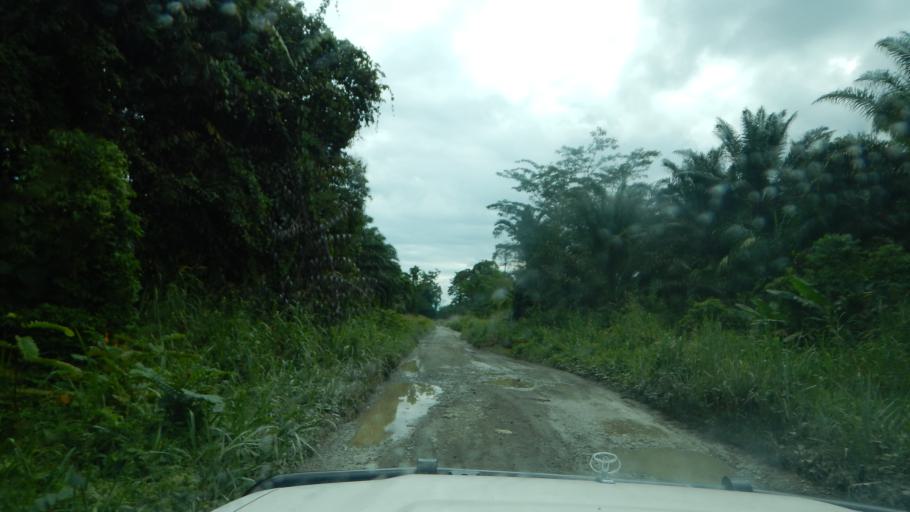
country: PG
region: Northern Province
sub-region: Sohe
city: Kokoda
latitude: -8.9179
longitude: 147.9422
